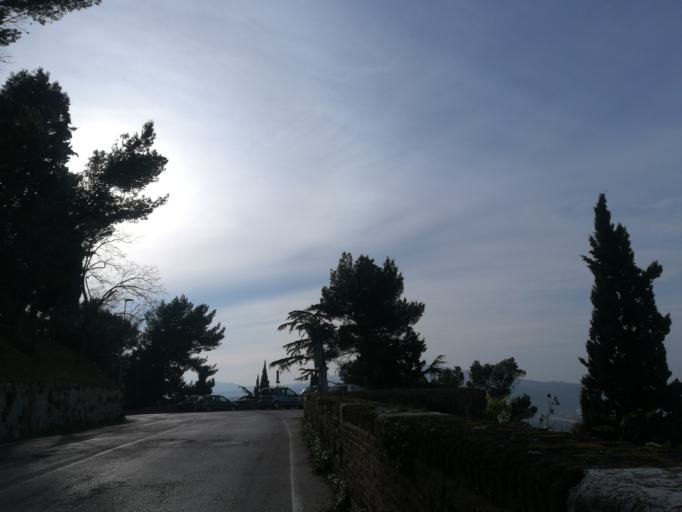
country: IT
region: The Marches
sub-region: Provincia di Ancona
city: Le Grazie di Ancona
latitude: 43.6141
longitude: 13.5073
